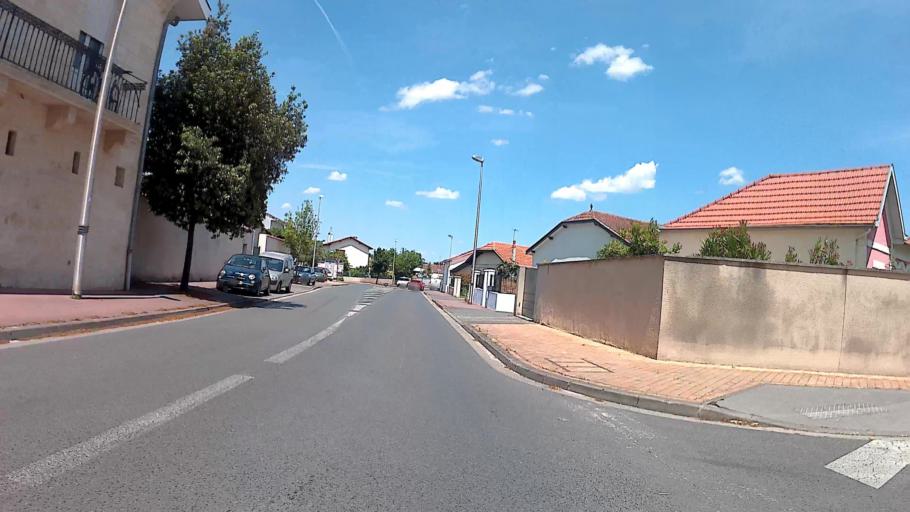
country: FR
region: Aquitaine
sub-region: Departement de la Gironde
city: Talence
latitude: 44.8008
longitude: -0.5757
